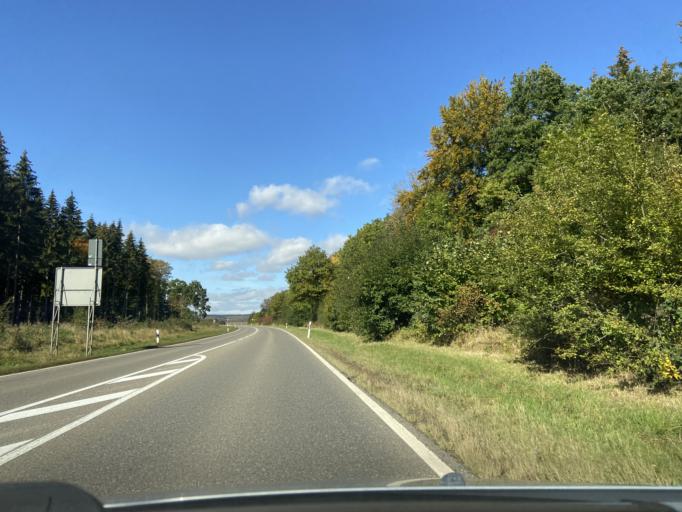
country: DE
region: Baden-Wuerttemberg
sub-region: Tuebingen Region
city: Sigmaringen
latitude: 48.0669
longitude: 9.2243
